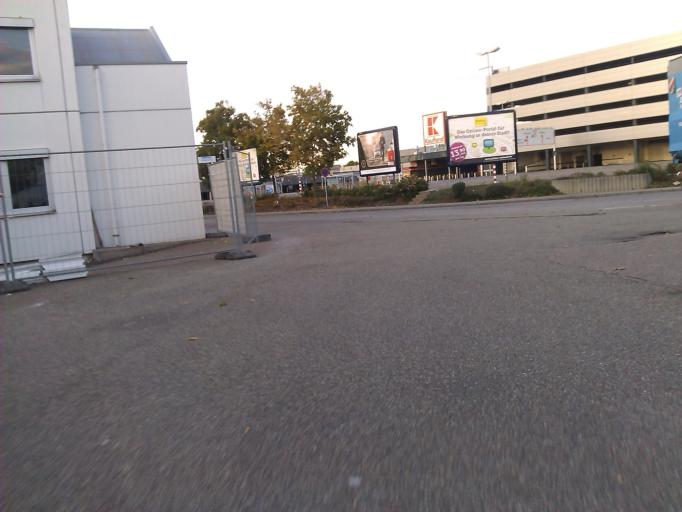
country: DE
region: Baden-Wuerttemberg
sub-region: Regierungsbezirk Stuttgart
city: Neckarsulm
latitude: 49.1697
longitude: 9.2211
